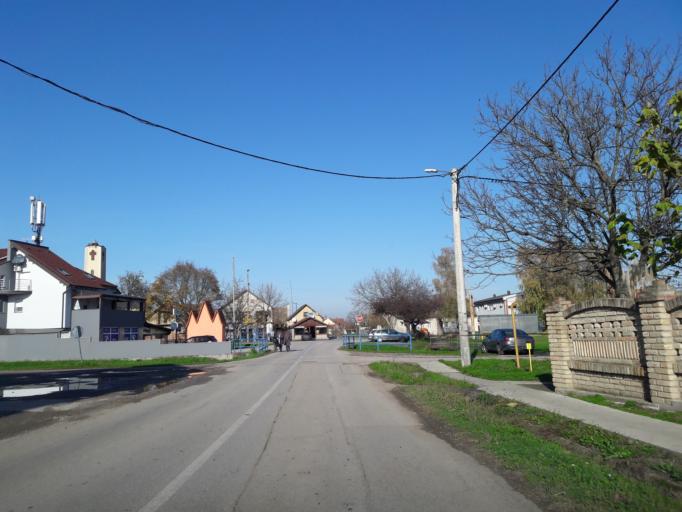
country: HR
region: Vukovarsko-Srijemska
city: Vodinci
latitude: 45.2752
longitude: 18.6107
